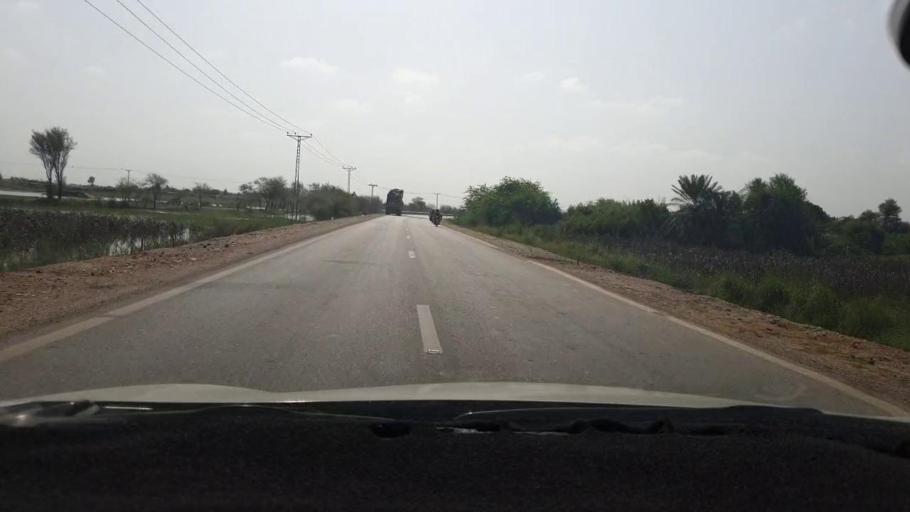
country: PK
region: Sindh
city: Mirpur Khas
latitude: 25.7589
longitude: 69.0822
